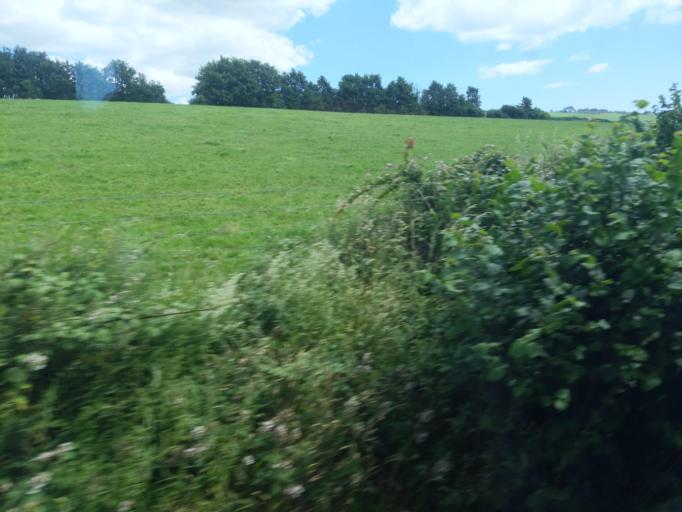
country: GB
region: England
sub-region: Cornwall
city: Lostwithiel
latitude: 50.3760
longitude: -4.6823
